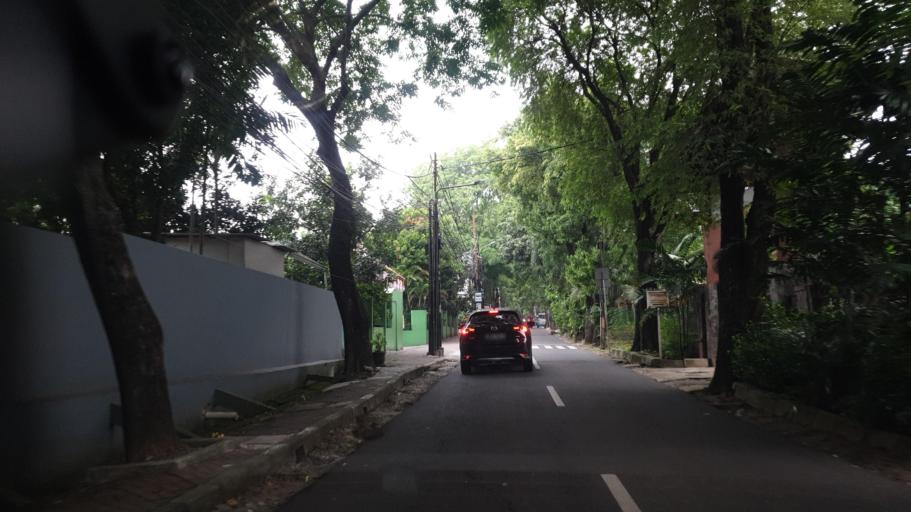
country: ID
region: West Java
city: Pamulang
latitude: -6.3035
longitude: 106.7777
